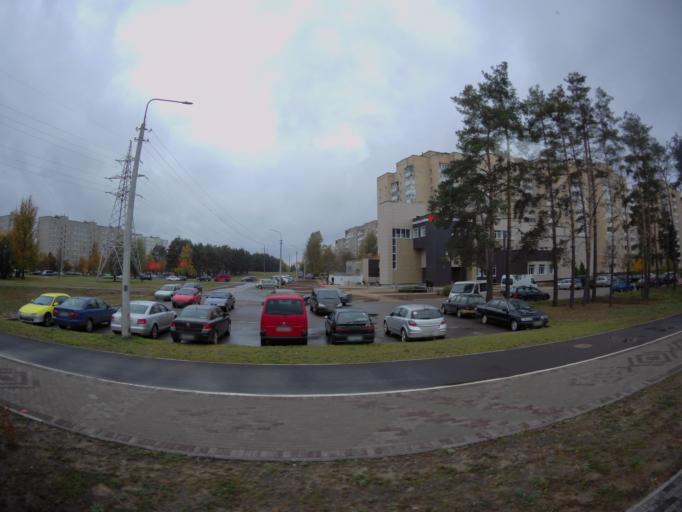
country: BY
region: Minsk
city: Horad Barysaw
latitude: 54.2038
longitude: 28.4824
